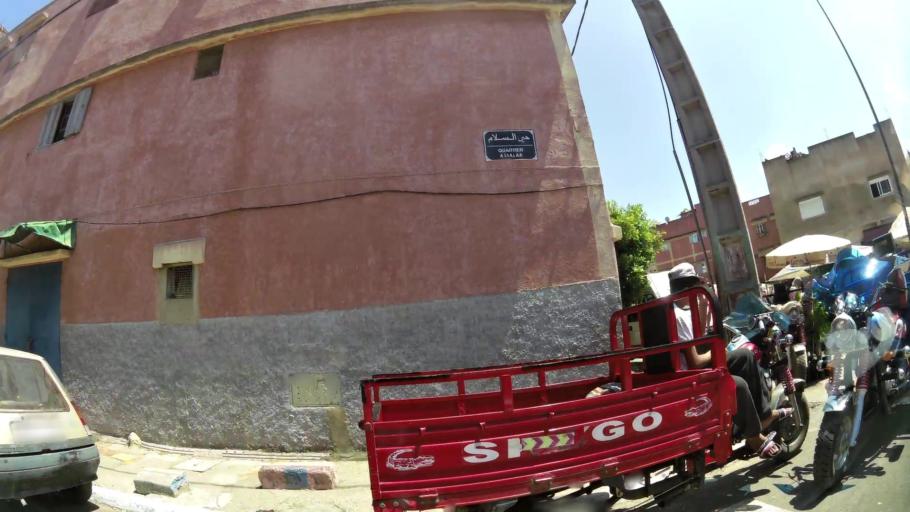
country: MA
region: Gharb-Chrarda-Beni Hssen
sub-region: Kenitra Province
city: Kenitra
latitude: 34.2566
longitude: -6.5573
